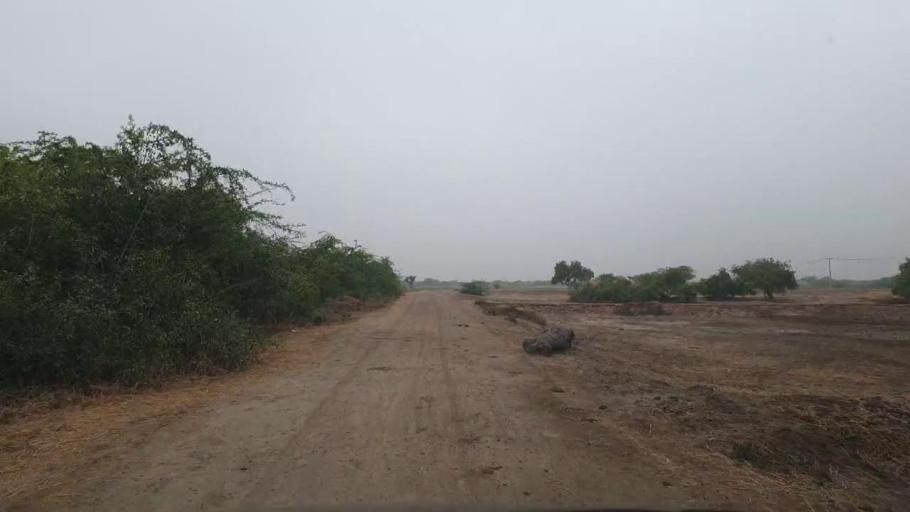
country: PK
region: Sindh
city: Badin
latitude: 24.6003
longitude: 68.6597
